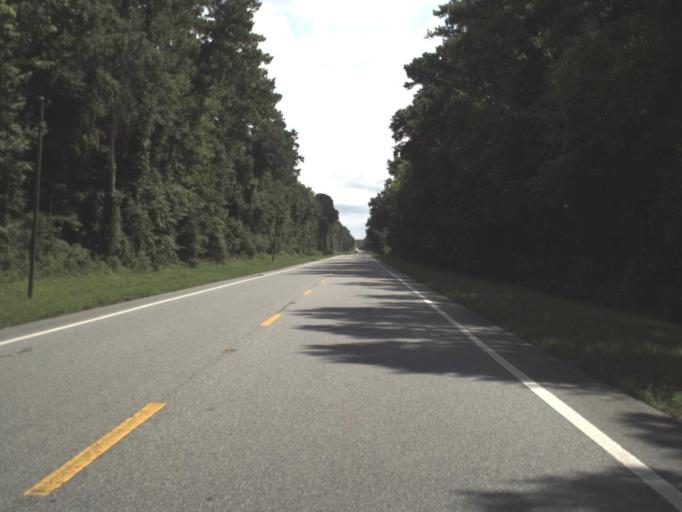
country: US
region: Florida
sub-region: Hernando County
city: Ridge Manor
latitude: 28.5147
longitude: -82.1048
